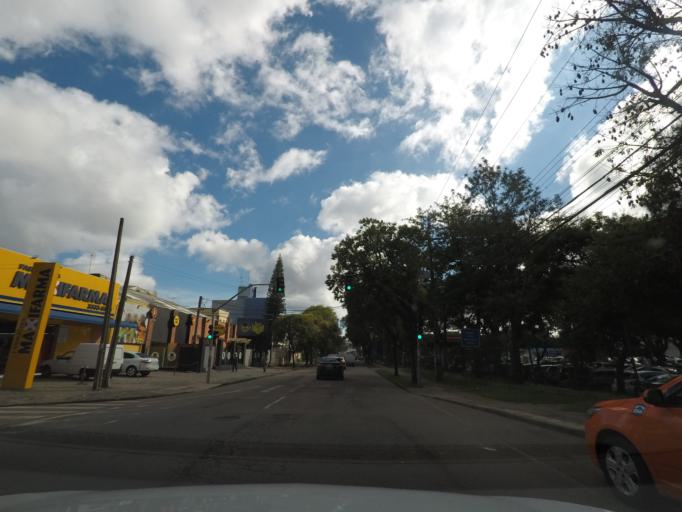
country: BR
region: Parana
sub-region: Curitiba
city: Curitiba
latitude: -25.4501
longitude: -49.2530
